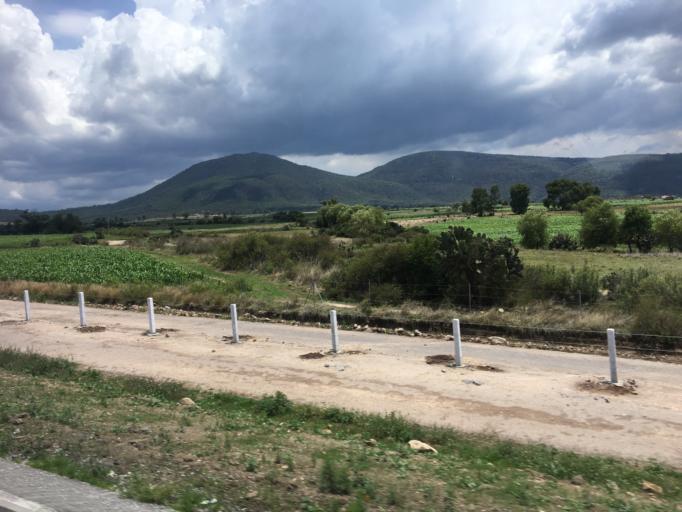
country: MX
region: Queretaro
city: Huimilpan
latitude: 20.3702
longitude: -100.3161
